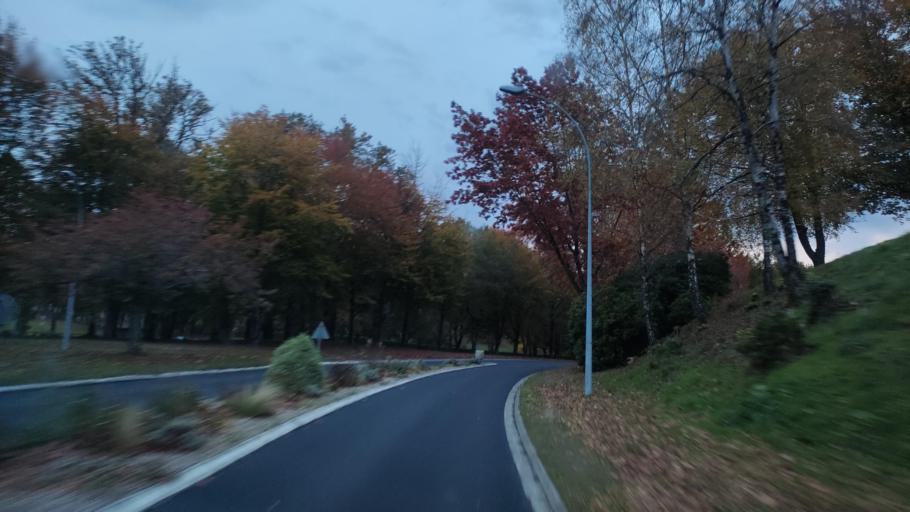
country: FR
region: Limousin
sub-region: Departement de la Haute-Vienne
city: Ambazac
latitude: 45.9498
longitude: 1.3935
